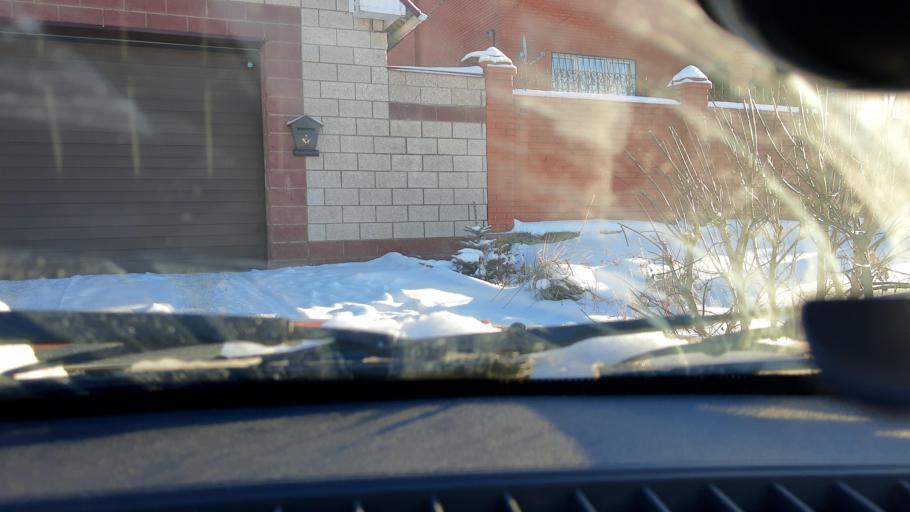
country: RU
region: Bashkortostan
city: Ufa
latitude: 54.6002
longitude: 55.9401
